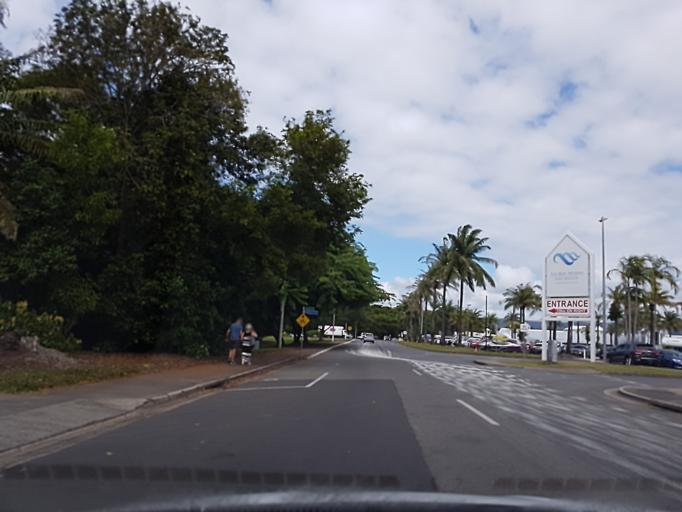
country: AU
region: Queensland
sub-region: Cairns
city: Port Douglas
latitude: -16.4830
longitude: 145.4614
